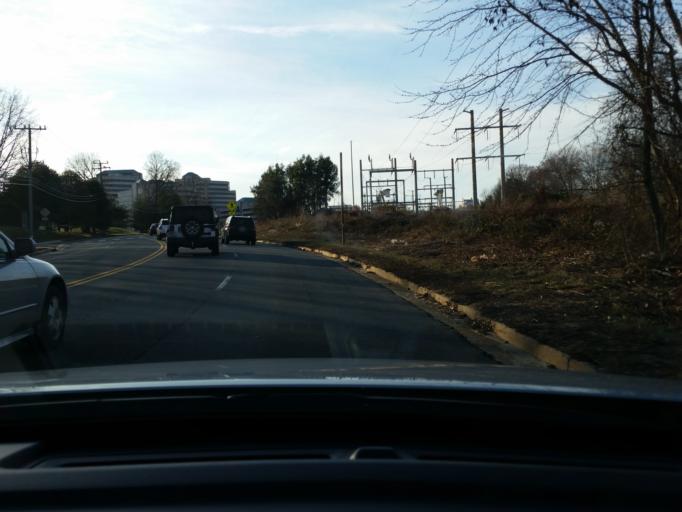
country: US
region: Virginia
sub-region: Fairfax County
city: Reston
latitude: 38.9521
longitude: -77.3432
